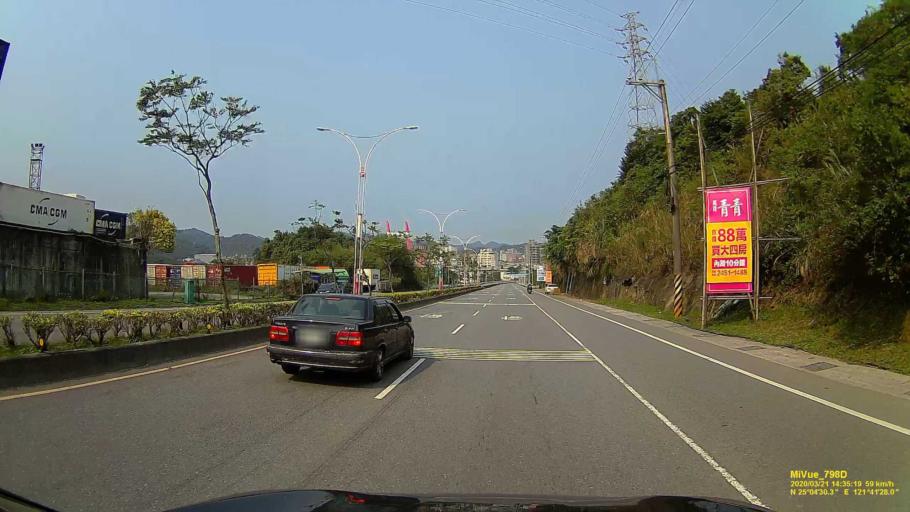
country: TW
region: Taiwan
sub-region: Keelung
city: Keelung
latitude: 25.0751
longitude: 121.6911
